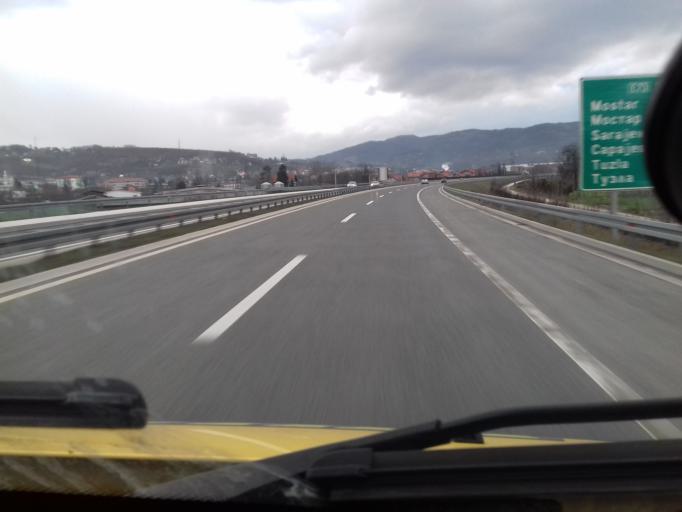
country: BA
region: Federation of Bosnia and Herzegovina
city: Ilijas
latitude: 43.9649
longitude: 18.2570
